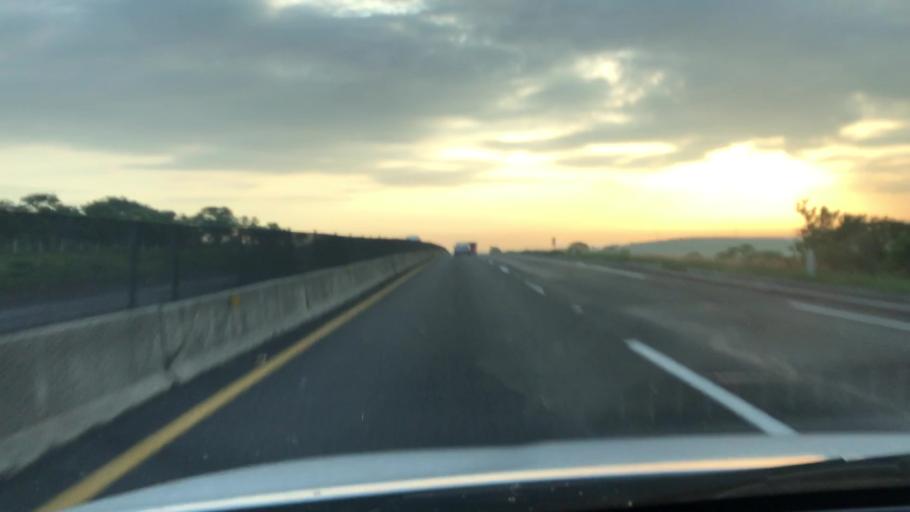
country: MX
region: Jalisco
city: Zapotlanejo
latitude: 20.6900
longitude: -103.0026
